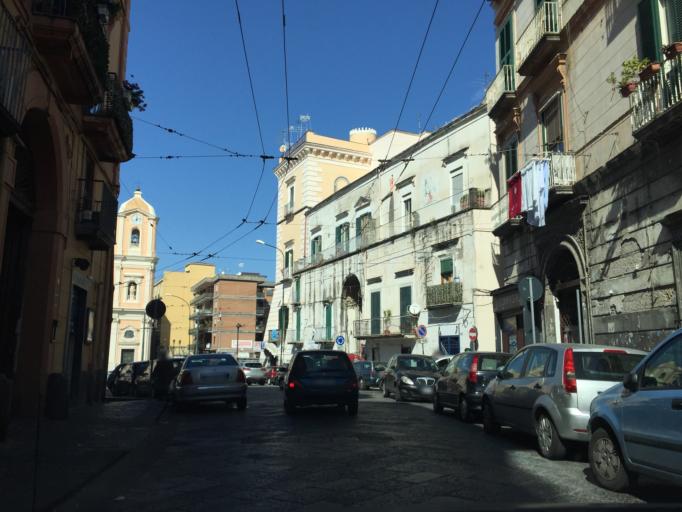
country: IT
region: Campania
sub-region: Provincia di Napoli
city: Portici
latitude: 40.8137
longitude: 14.3397
